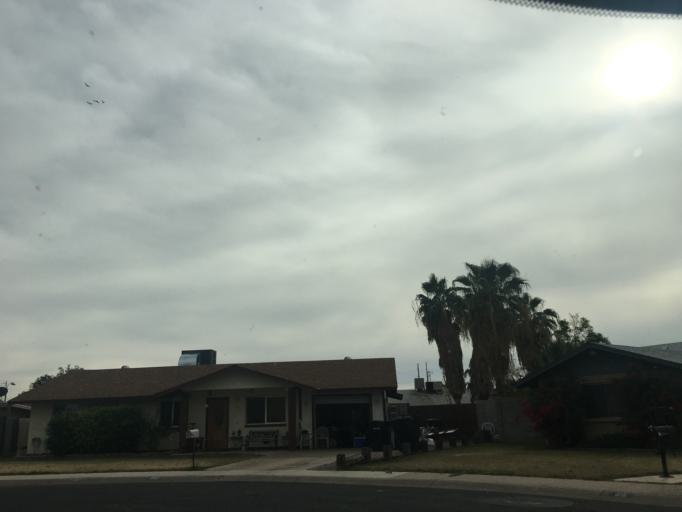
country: US
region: Arizona
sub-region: Maricopa County
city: Gilbert
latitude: 33.3615
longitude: -111.7980
